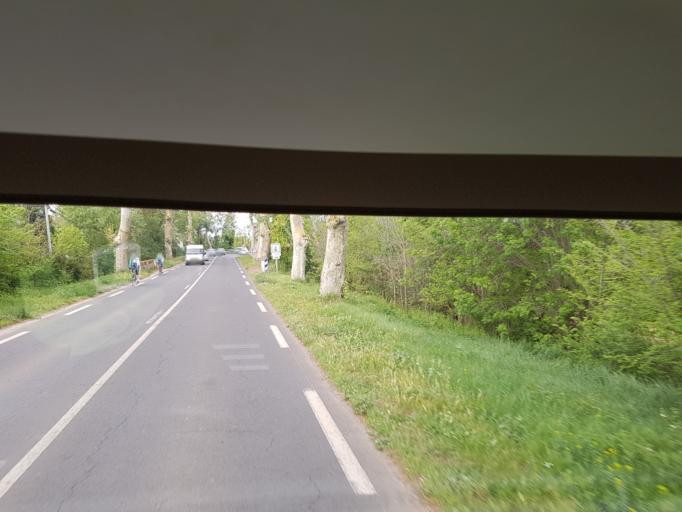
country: FR
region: Languedoc-Roussillon
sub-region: Departement de l'Herault
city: Agde
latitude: 43.3250
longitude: 3.4792
